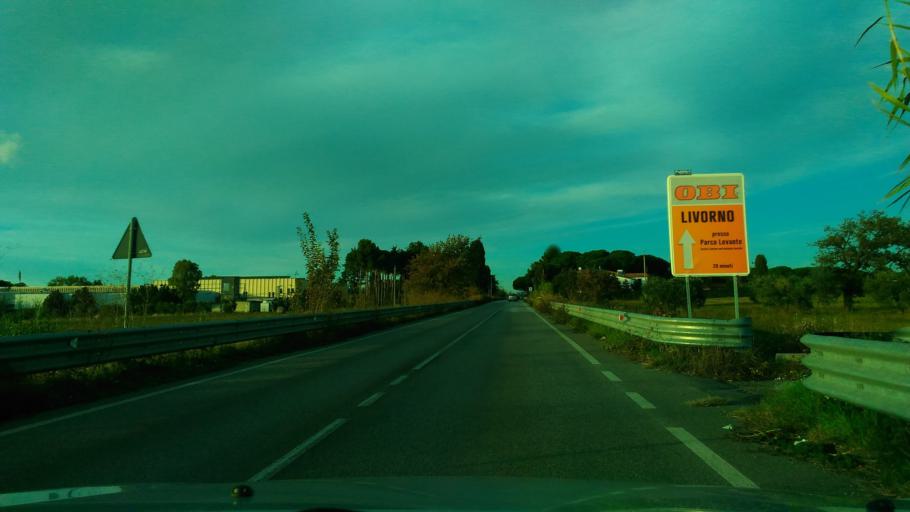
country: IT
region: Tuscany
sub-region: Provincia di Livorno
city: S.P. in Palazzi
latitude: 43.3432
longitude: 10.5046
